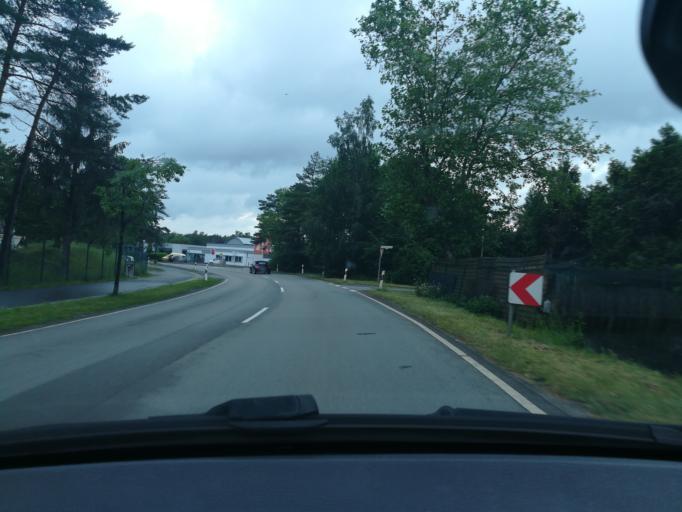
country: DE
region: North Rhine-Westphalia
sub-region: Regierungsbezirk Detmold
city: Oerlinghausen
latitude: 51.9346
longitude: 8.6582
